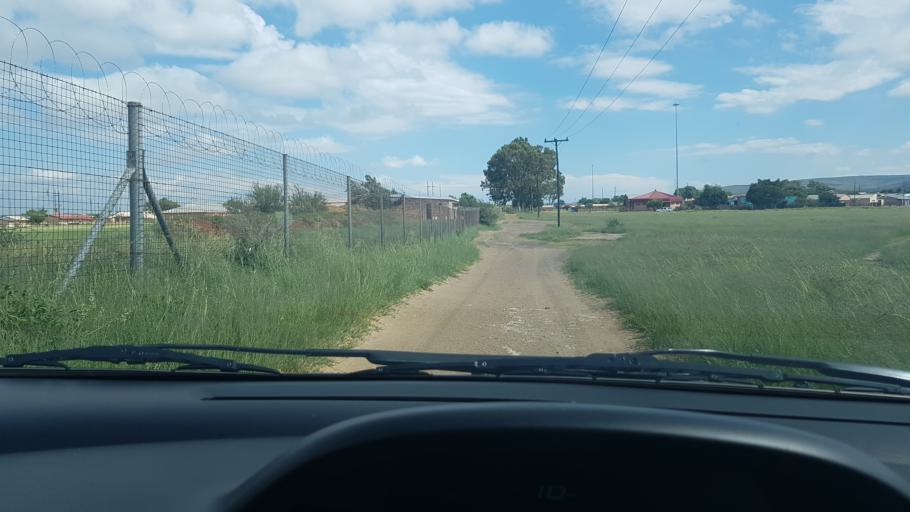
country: ZA
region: Northern Cape
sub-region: Siyanda District Municipality
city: Danielskuil
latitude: -28.1877
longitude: 23.5387
